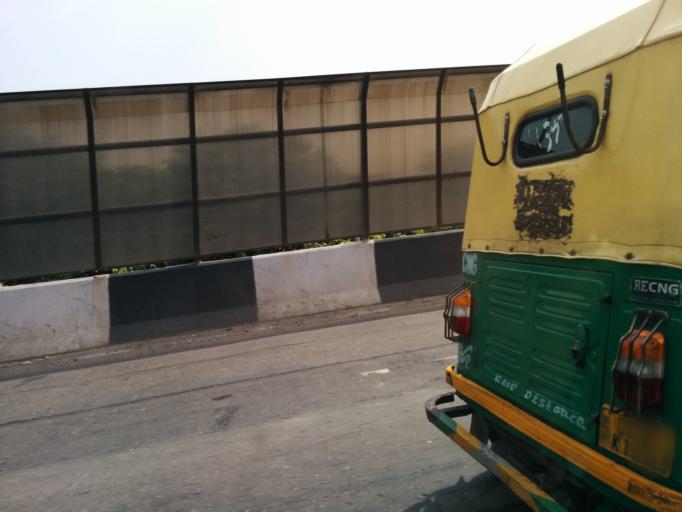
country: IN
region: NCT
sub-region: New Delhi
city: New Delhi
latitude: 28.5509
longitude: 77.1835
